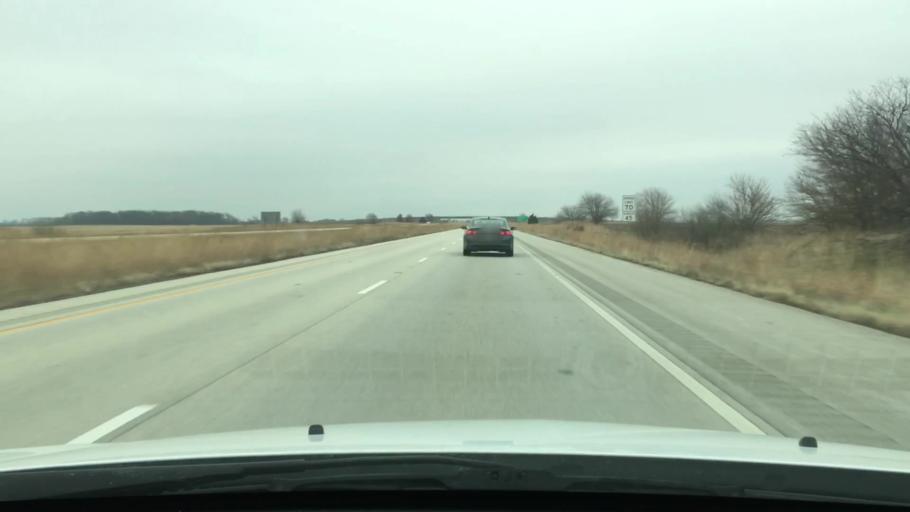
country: US
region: Illinois
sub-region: Sangamon County
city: New Berlin
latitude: 39.7401
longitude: -89.9113
